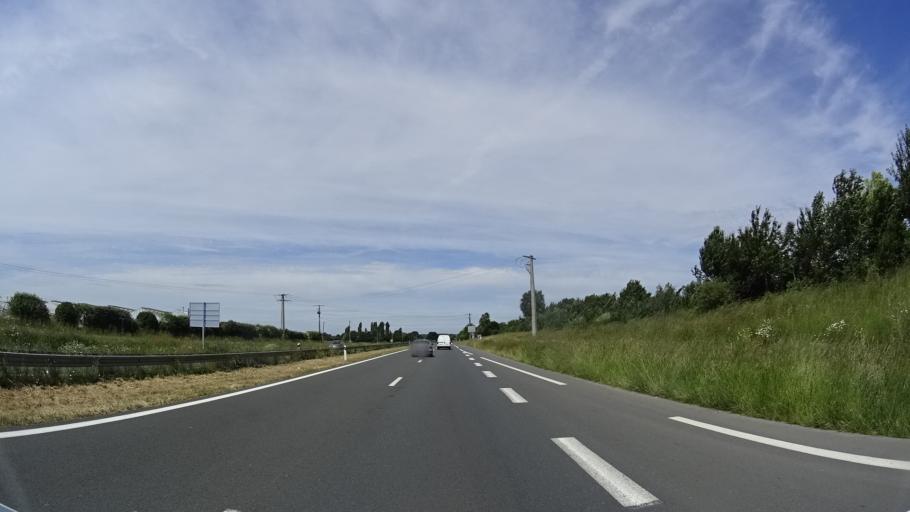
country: FR
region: Pays de la Loire
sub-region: Departement de Maine-et-Loire
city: Grez-Neuville
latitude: 47.6146
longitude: -0.7127
